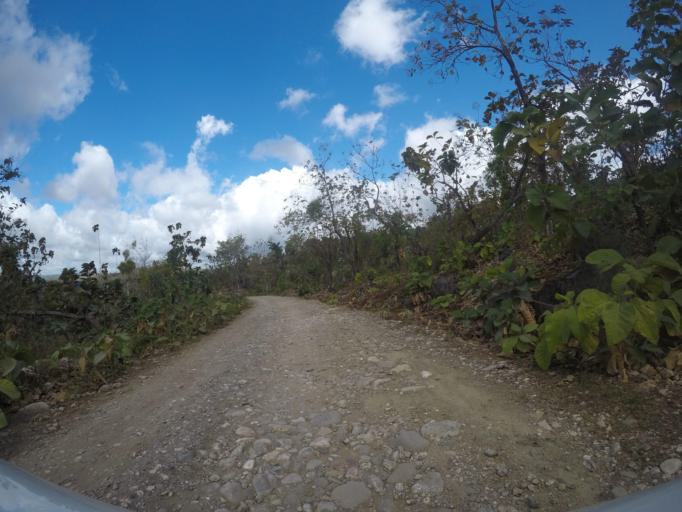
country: TL
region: Lautem
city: Lospalos
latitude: -8.5347
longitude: 126.8391
